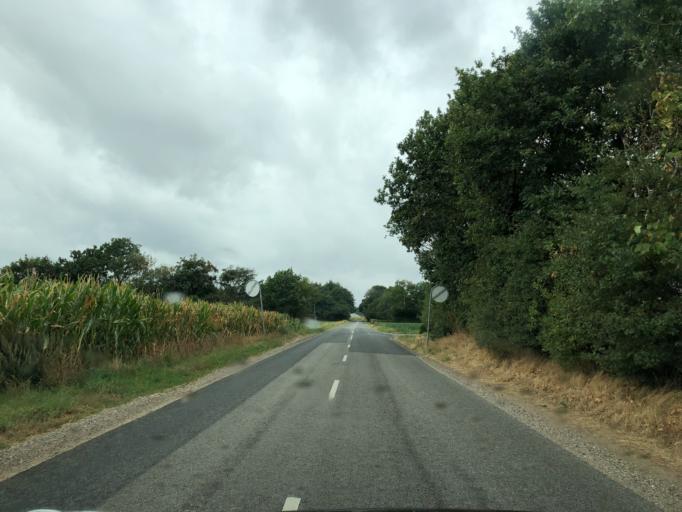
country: DK
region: Central Jutland
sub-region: Holstebro Kommune
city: Ulfborg
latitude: 56.1446
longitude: 8.4059
